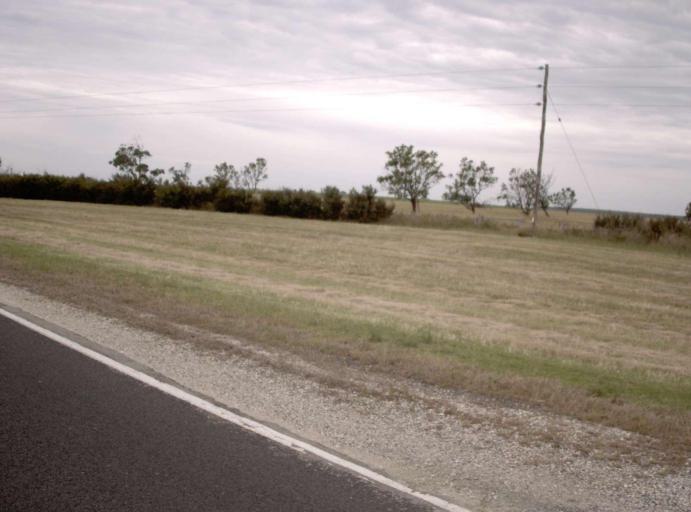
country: AU
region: Victoria
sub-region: Wellington
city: Sale
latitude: -38.1968
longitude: 147.2933
